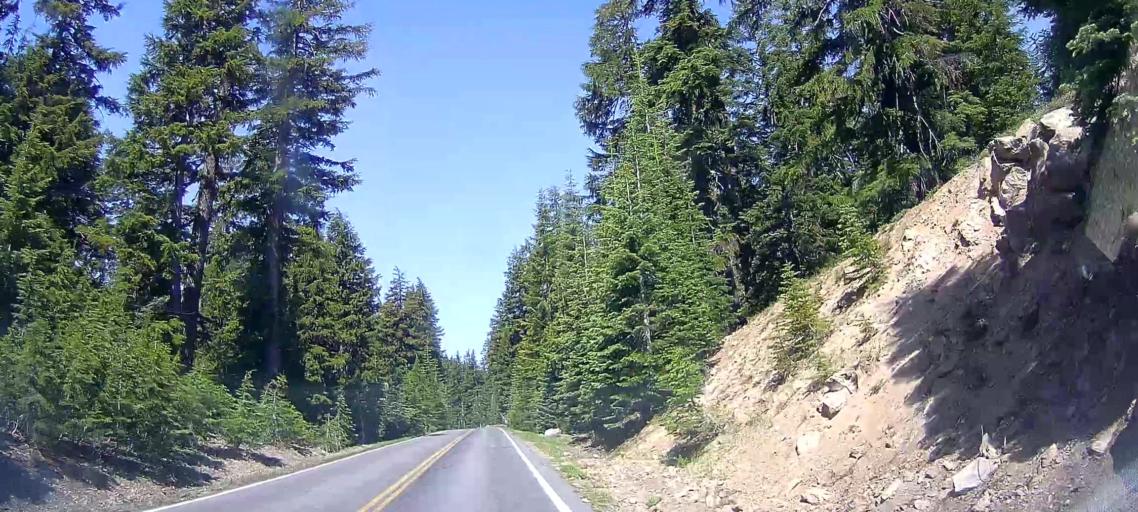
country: US
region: Oregon
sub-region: Klamath County
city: Klamath Falls
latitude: 42.8802
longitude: -122.1168
